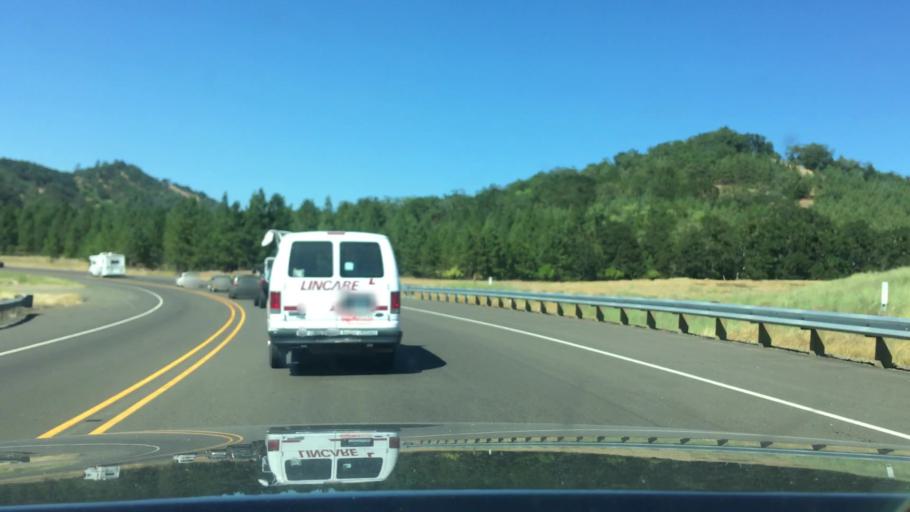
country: US
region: Oregon
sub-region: Douglas County
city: Green
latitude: 43.1540
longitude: -123.3634
